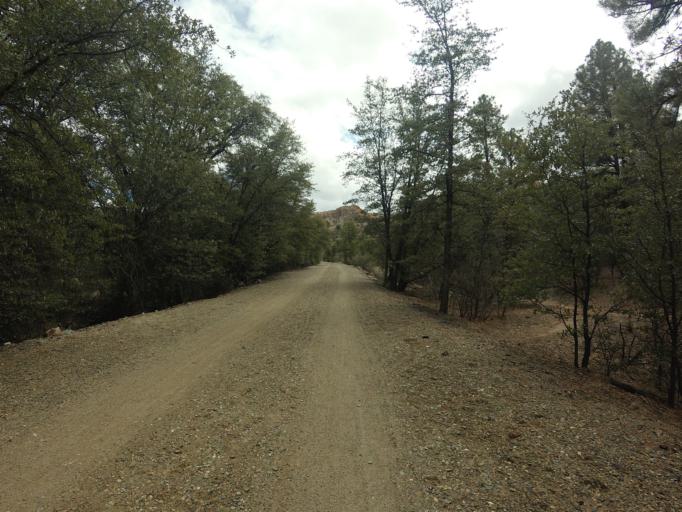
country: US
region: Arizona
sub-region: Yavapai County
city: Prescott Valley
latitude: 34.6056
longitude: -112.3962
